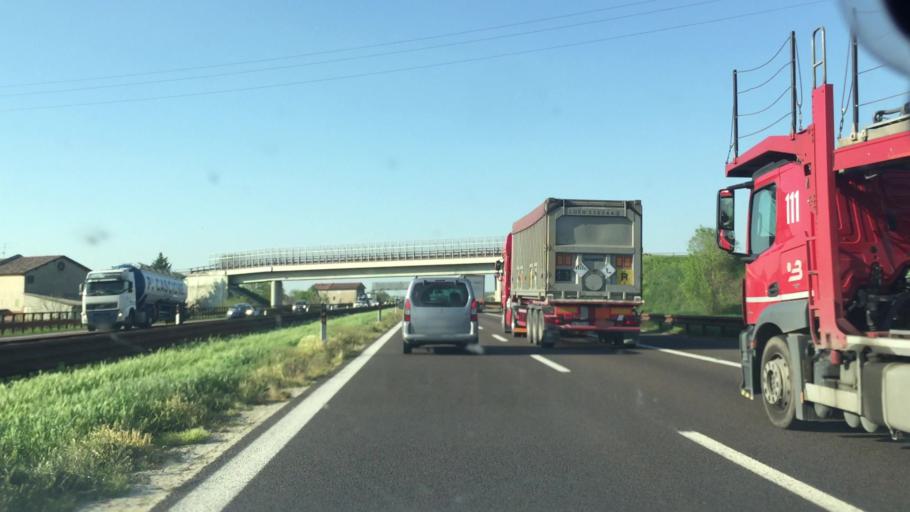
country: IT
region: Emilia-Romagna
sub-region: Provincia di Modena
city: Santa Croce Scuole
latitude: 44.7344
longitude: 10.8443
